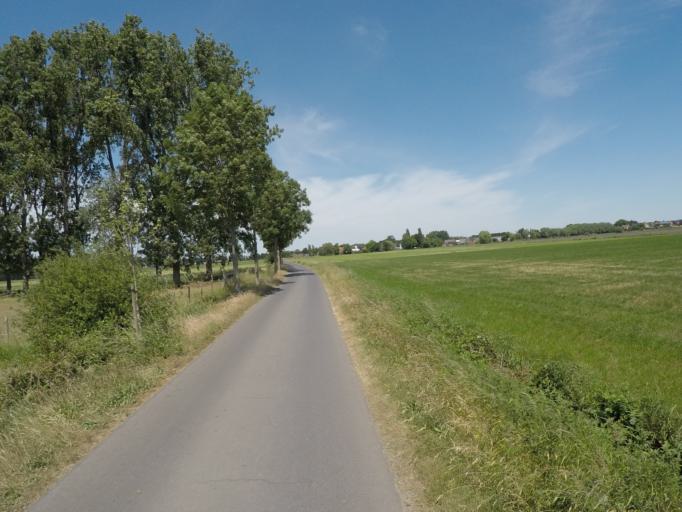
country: BE
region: Flanders
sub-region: Provincie Antwerpen
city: Wuustwezel
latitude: 51.3946
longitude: 4.6258
